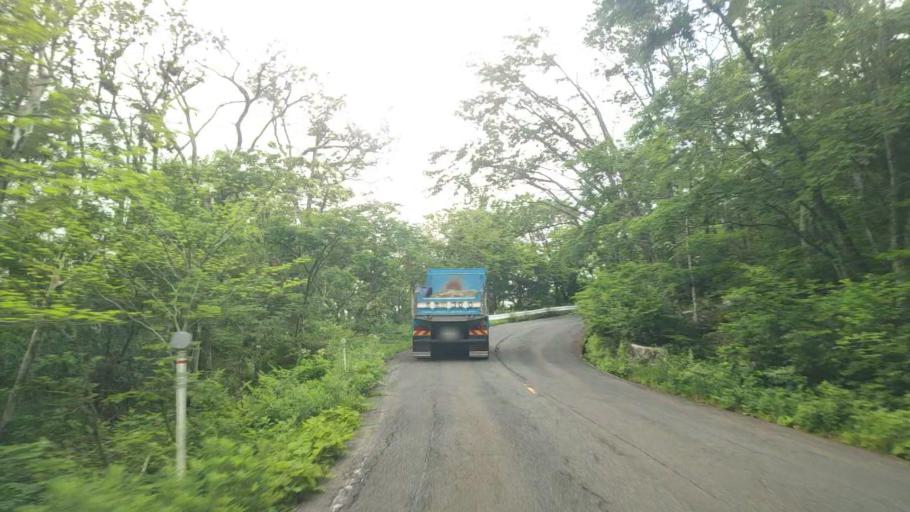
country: JP
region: Tottori
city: Yonago
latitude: 35.3823
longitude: 133.5236
